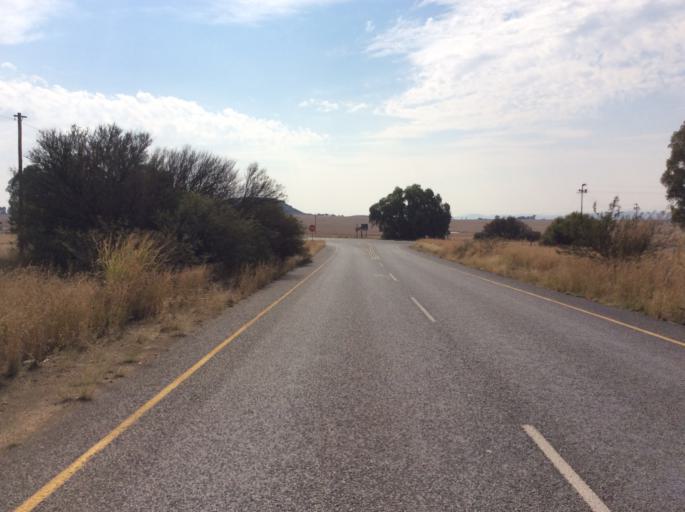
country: ZA
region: Orange Free State
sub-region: Xhariep District Municipality
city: Dewetsdorp
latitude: -29.5636
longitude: 26.6661
